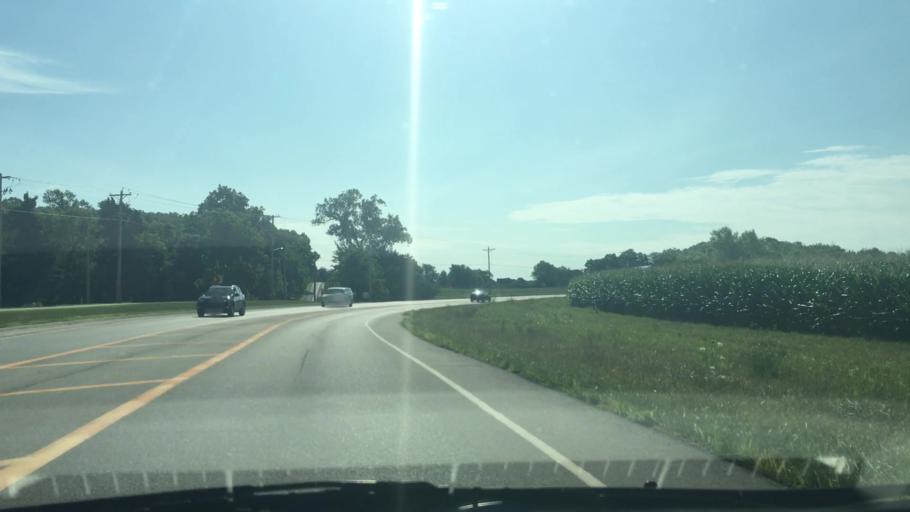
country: US
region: Iowa
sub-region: Johnson County
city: North Liberty
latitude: 41.7335
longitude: -91.5683
